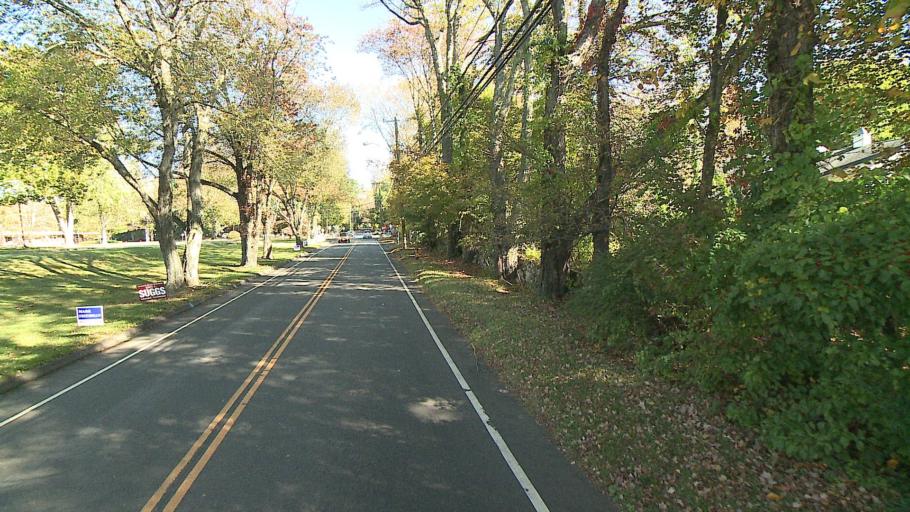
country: US
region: Connecticut
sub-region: Fairfield County
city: Westport
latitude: 41.1753
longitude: -73.3484
